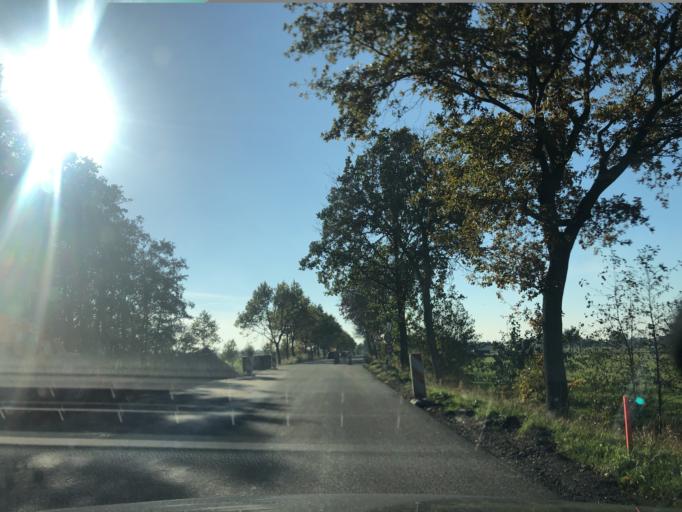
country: DE
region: Lower Saxony
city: Lemwerder
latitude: 53.1574
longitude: 8.5576
